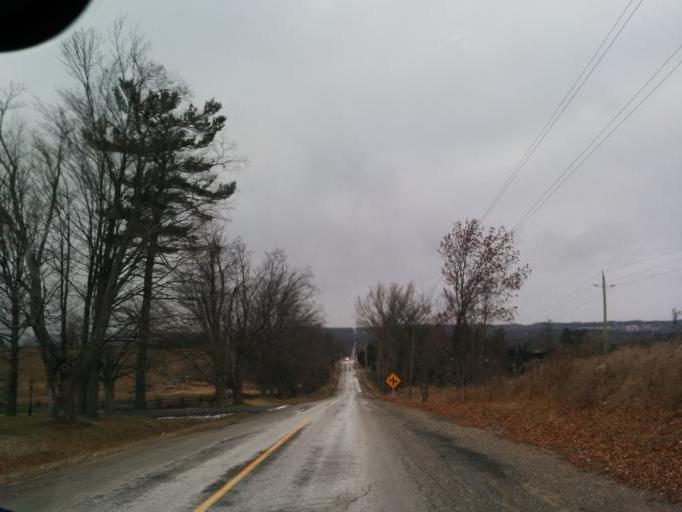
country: CA
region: Ontario
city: Orangeville
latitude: 43.8047
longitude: -79.9447
